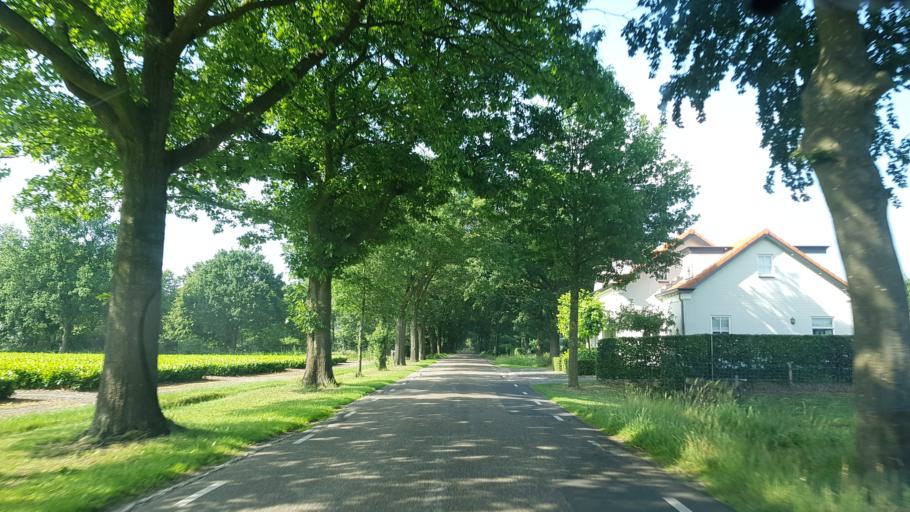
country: NL
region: North Brabant
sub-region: Gemeente Breda
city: Hoge Vucht
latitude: 51.6234
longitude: 4.8213
